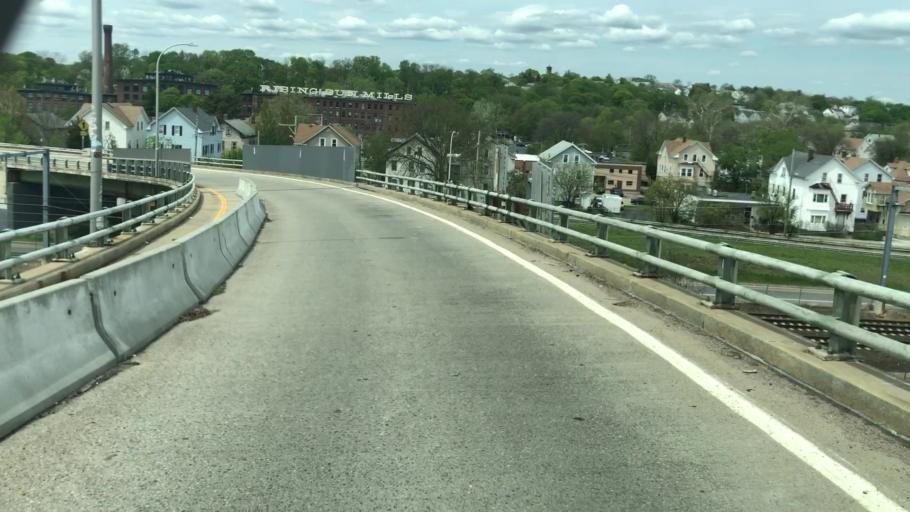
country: US
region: Rhode Island
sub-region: Providence County
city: Providence
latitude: 41.8206
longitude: -71.4368
